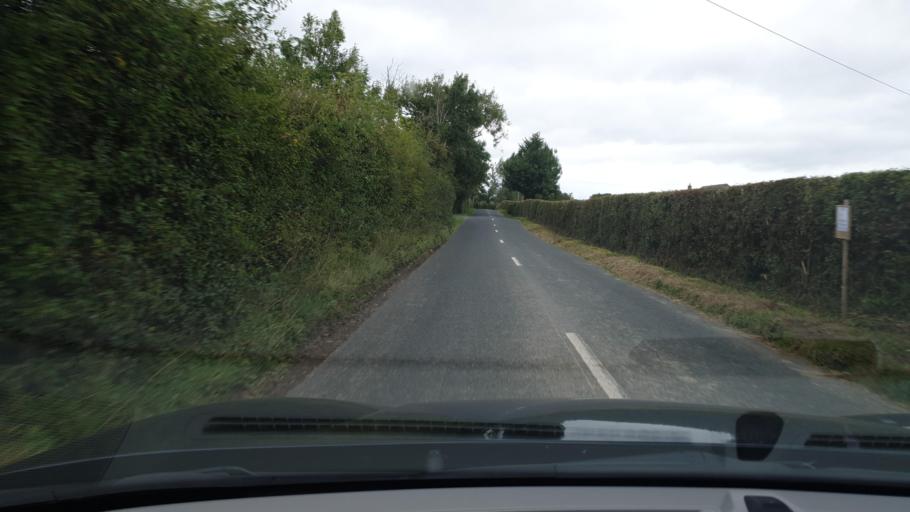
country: IE
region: Leinster
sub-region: Kildare
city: Clane
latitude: 53.3229
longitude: -6.6393
